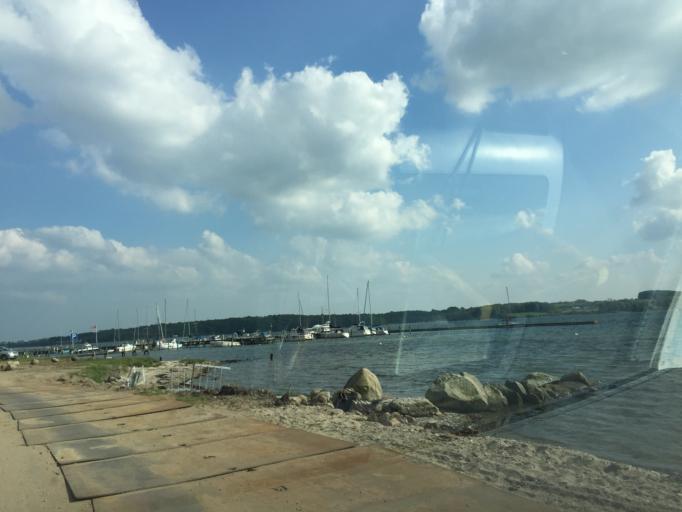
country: DK
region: South Denmark
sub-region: Aabenraa Kommune
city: Lojt Kirkeby
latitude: 55.1309
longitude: 9.4794
